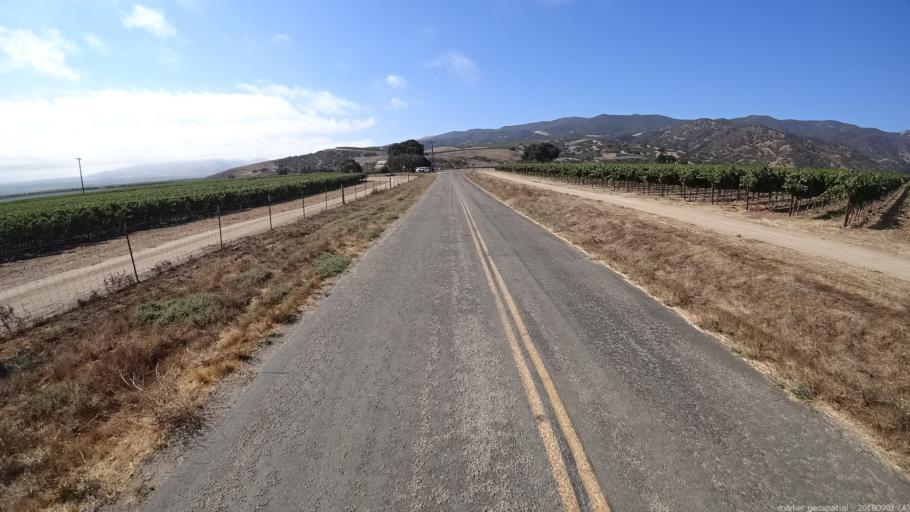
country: US
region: California
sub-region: Monterey County
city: Soledad
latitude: 36.3410
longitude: -121.3424
